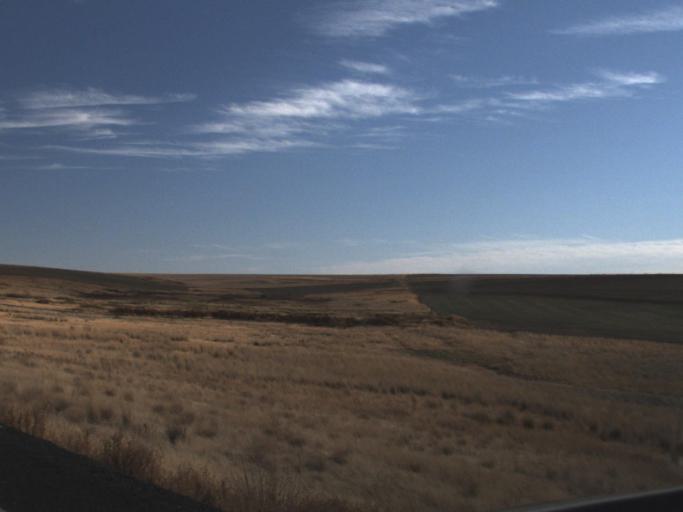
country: US
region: Washington
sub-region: Adams County
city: Ritzville
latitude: 47.3785
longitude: -118.6925
